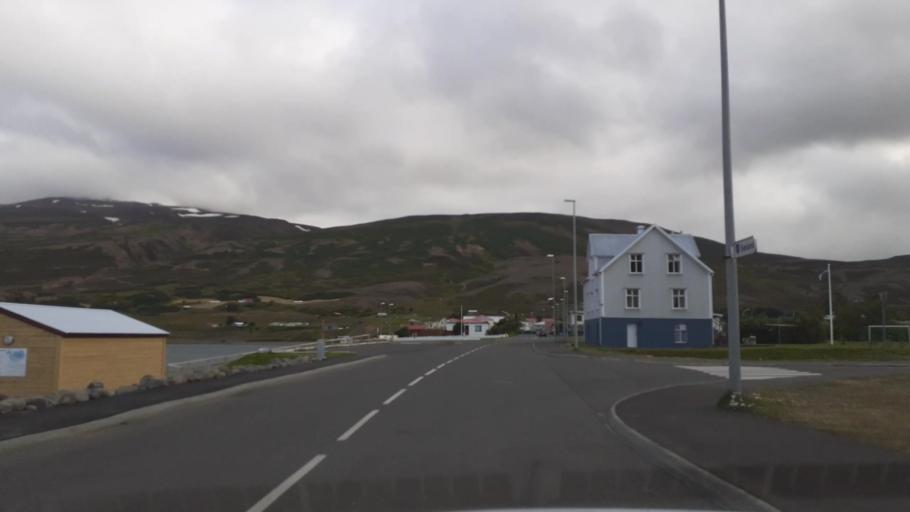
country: IS
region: Northeast
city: Akureyri
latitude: 65.9465
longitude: -18.1856
